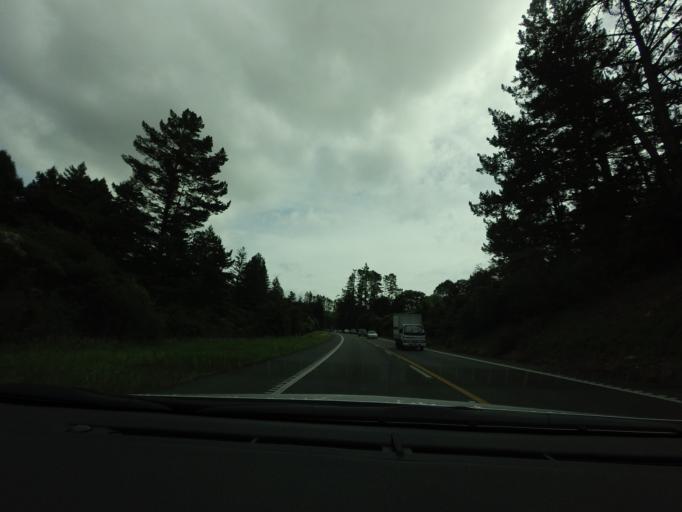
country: NZ
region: Auckland
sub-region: Auckland
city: Warkworth
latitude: -36.4500
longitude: 174.6521
